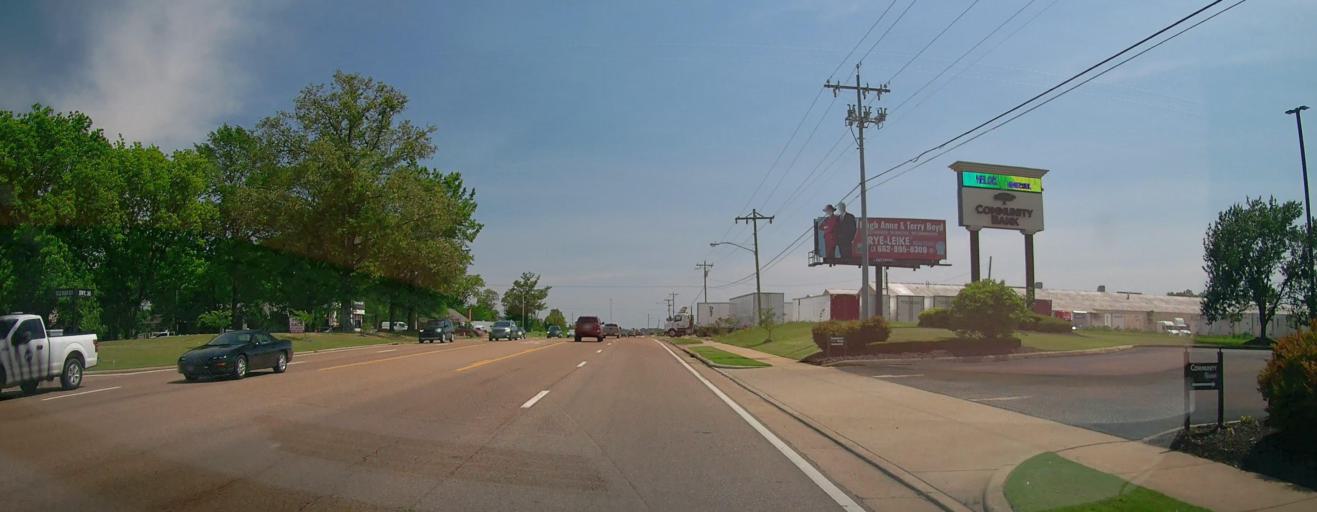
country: US
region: Mississippi
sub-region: De Soto County
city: Olive Branch
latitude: 34.9525
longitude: -89.8305
